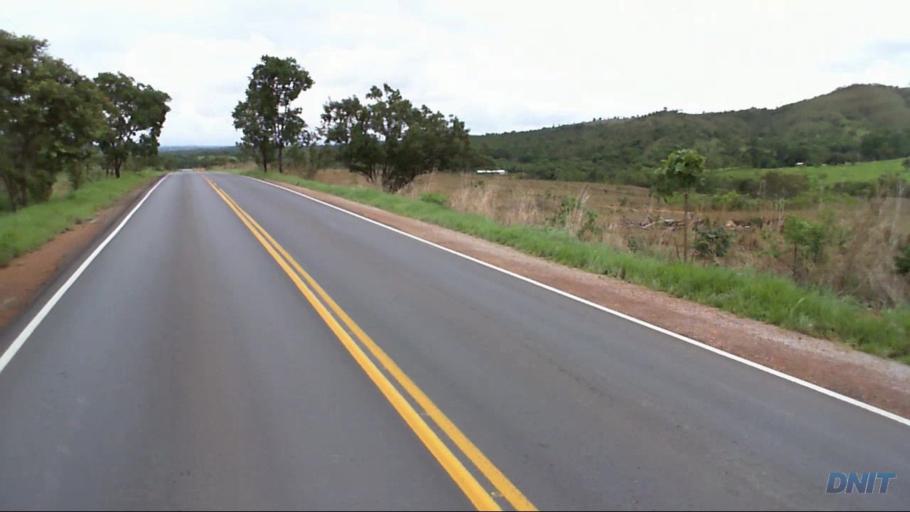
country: BR
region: Goias
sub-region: Padre Bernardo
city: Padre Bernardo
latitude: -15.4314
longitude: -48.1938
